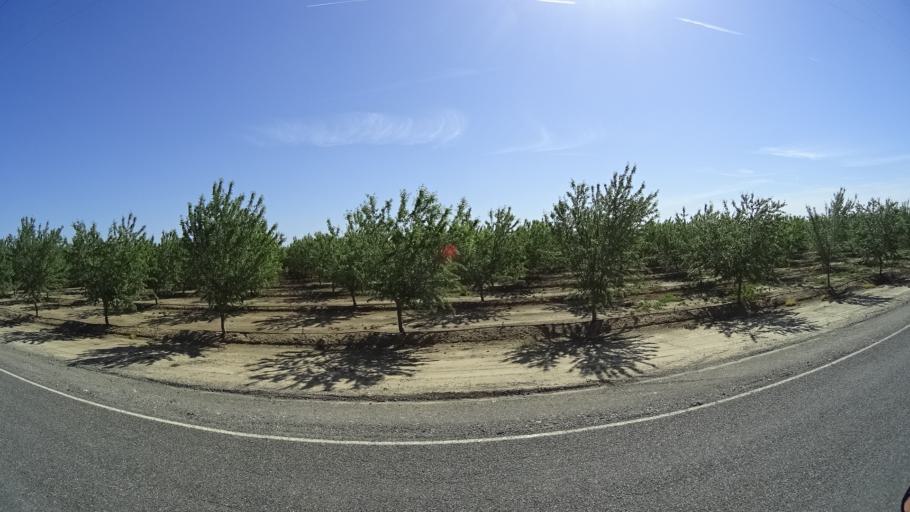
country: US
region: California
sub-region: Glenn County
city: Orland
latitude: 39.6412
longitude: -122.1786
